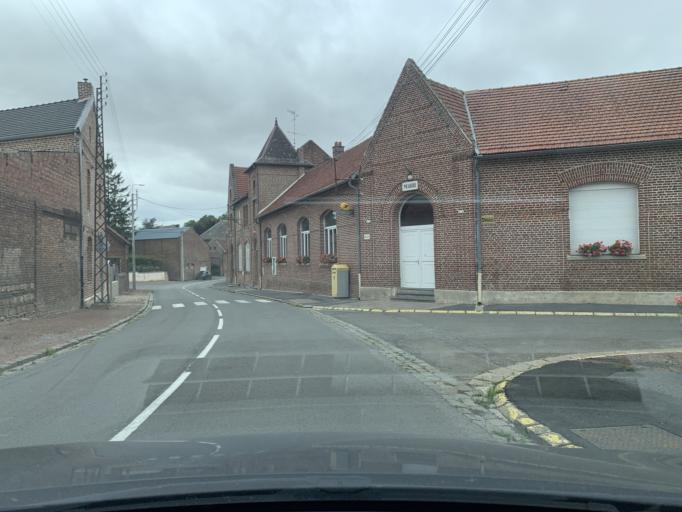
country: FR
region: Nord-Pas-de-Calais
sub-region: Departement du Nord
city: Fechain
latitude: 50.2351
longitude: 3.2129
